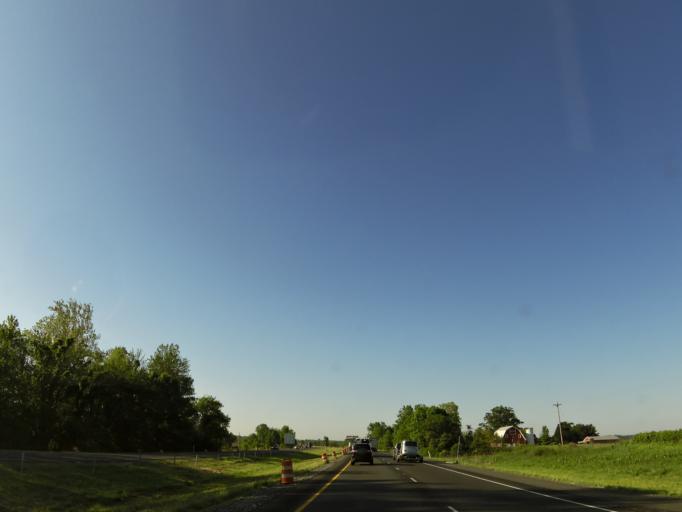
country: US
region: Indiana
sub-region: Jackson County
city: Seymour
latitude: 38.9413
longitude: -85.8432
